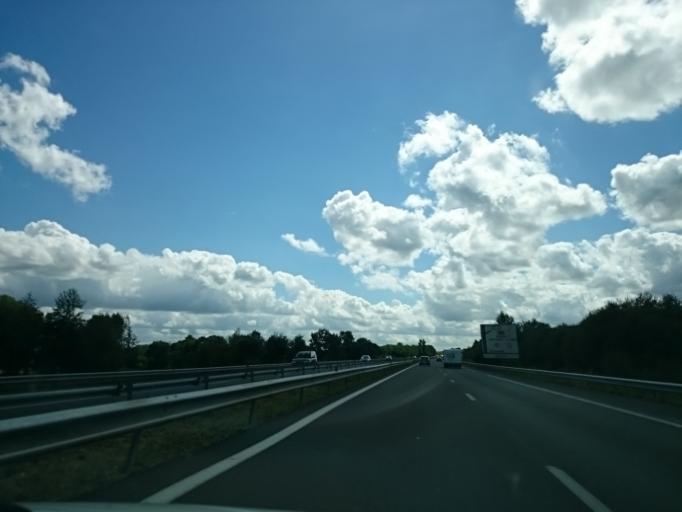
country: FR
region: Pays de la Loire
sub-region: Departement de Maine-et-Loire
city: Durtal
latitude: 47.6924
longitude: -0.2498
